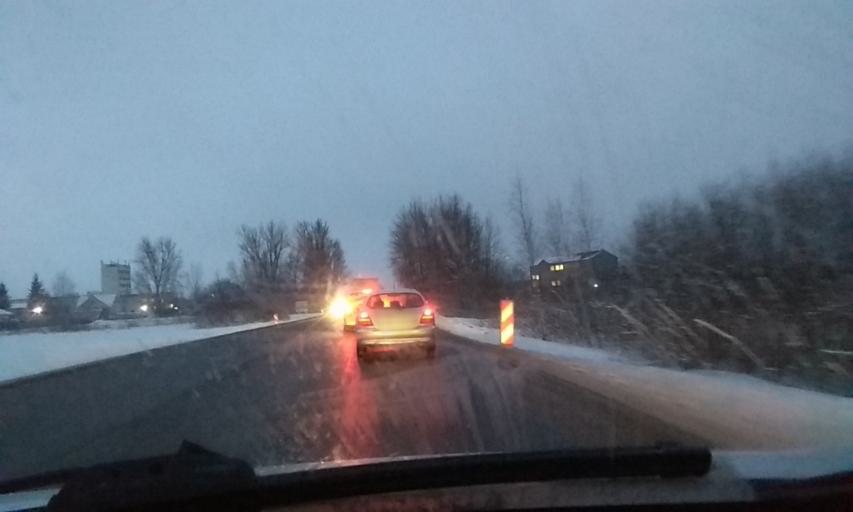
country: LT
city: Ramuciai
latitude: 54.9092
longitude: 24.0319
